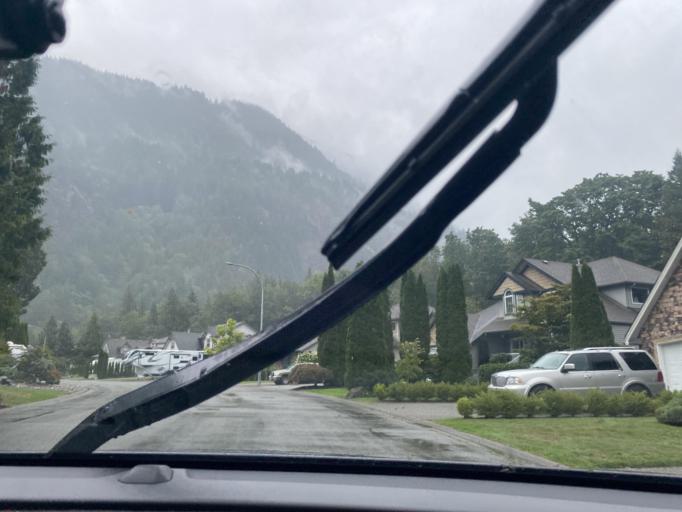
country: CA
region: British Columbia
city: Agassiz
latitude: 49.2983
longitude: -121.7761
